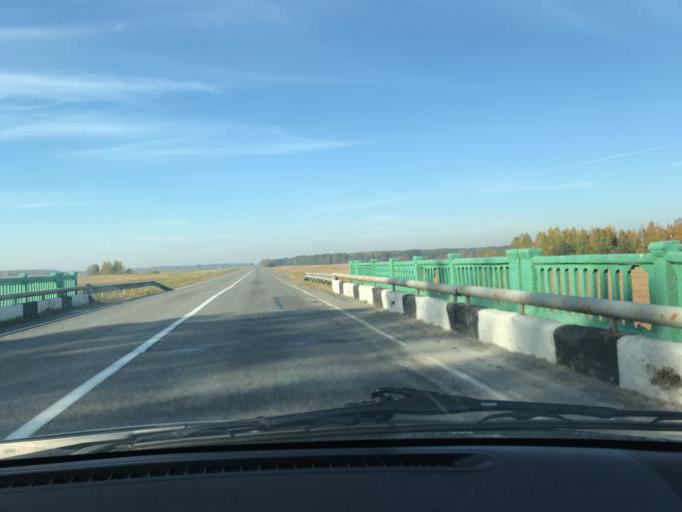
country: BY
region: Brest
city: Davyd-Haradok
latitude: 52.2422
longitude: 27.1845
